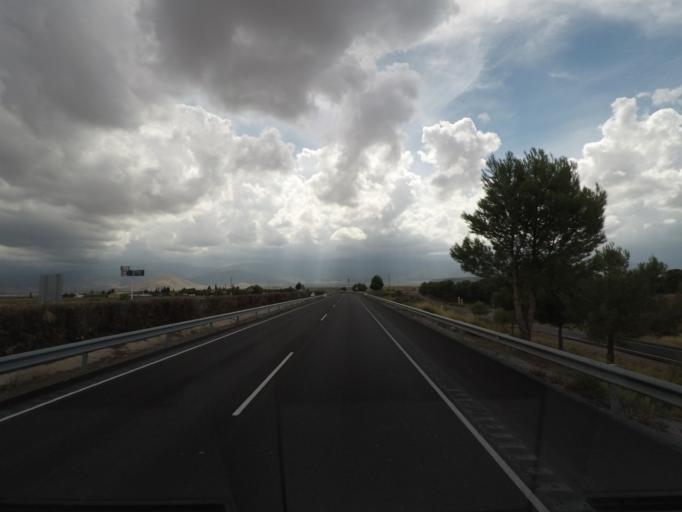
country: ES
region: Andalusia
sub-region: Provincia de Granada
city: Albunan
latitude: 37.2318
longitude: -3.0824
